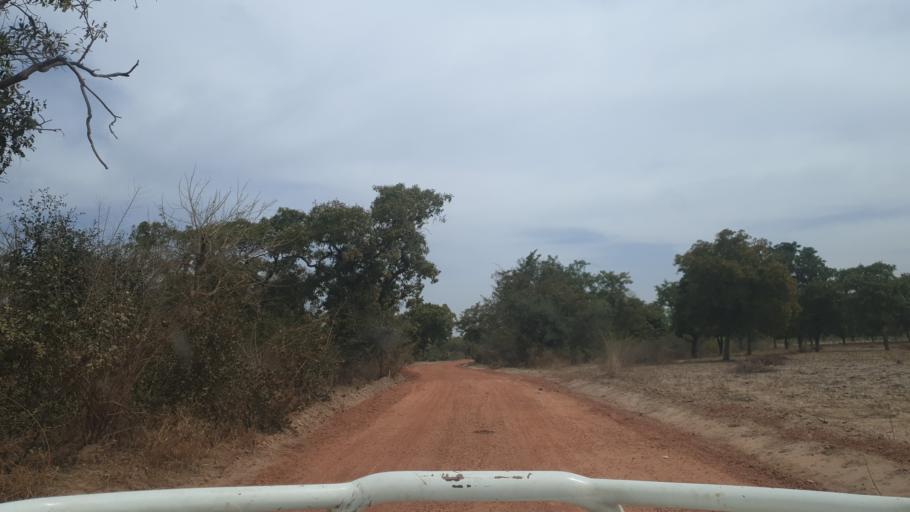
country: ML
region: Sikasso
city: Yorosso
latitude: 12.2345
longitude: -4.7458
